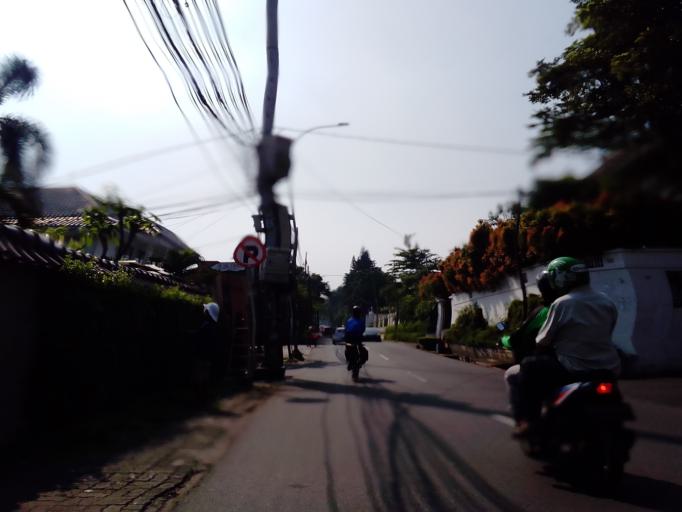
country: ID
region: Jakarta Raya
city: Jakarta
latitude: -6.2662
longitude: 106.8067
